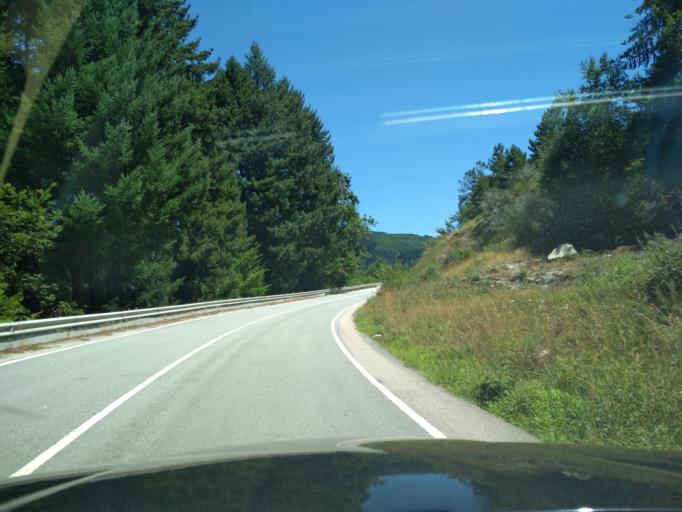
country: PT
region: Vila Real
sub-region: Ribeira de Pena
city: Ribeira de Pena
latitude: 41.5148
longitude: -7.7994
